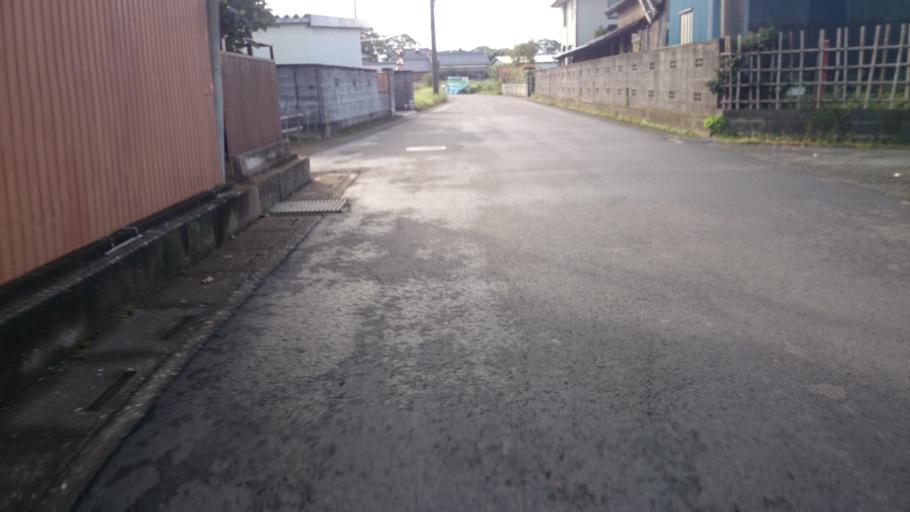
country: JP
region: Saitama
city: Kamifukuoka
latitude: 35.9070
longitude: 139.5671
